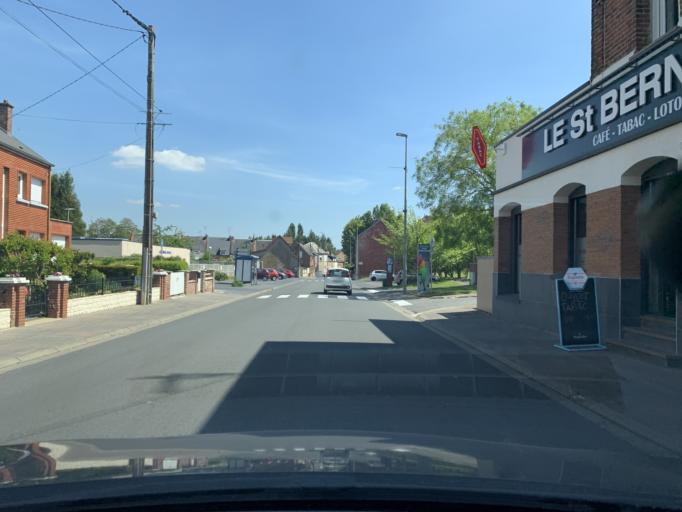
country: FR
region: Nord-Pas-de-Calais
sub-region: Departement du Nord
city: Caudry
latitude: 50.1247
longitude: 3.3984
